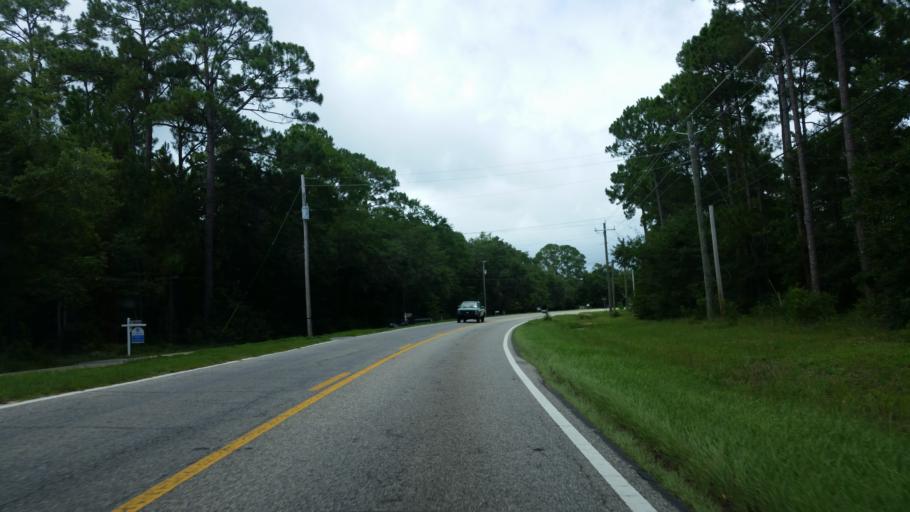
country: US
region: Florida
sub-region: Santa Rosa County
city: Holley
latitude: 30.4455
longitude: -86.9463
